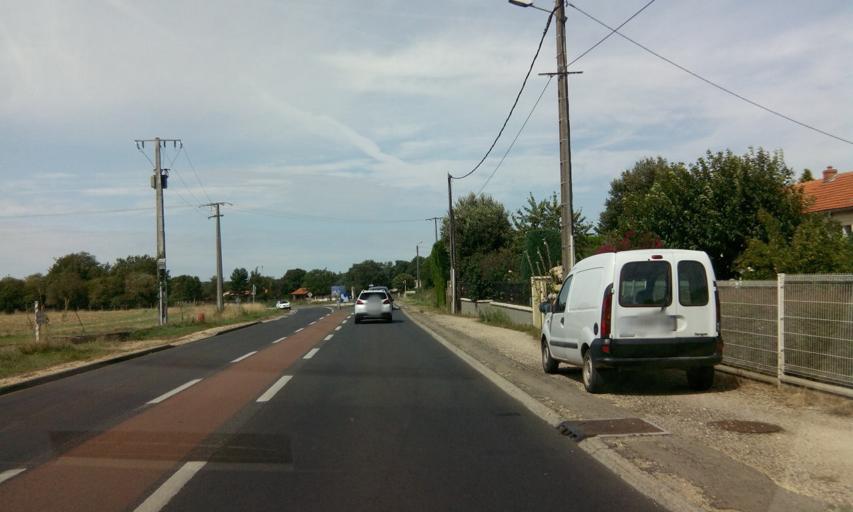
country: FR
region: Poitou-Charentes
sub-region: Departement de la Vienne
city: Civray
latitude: 46.1434
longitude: 0.2223
